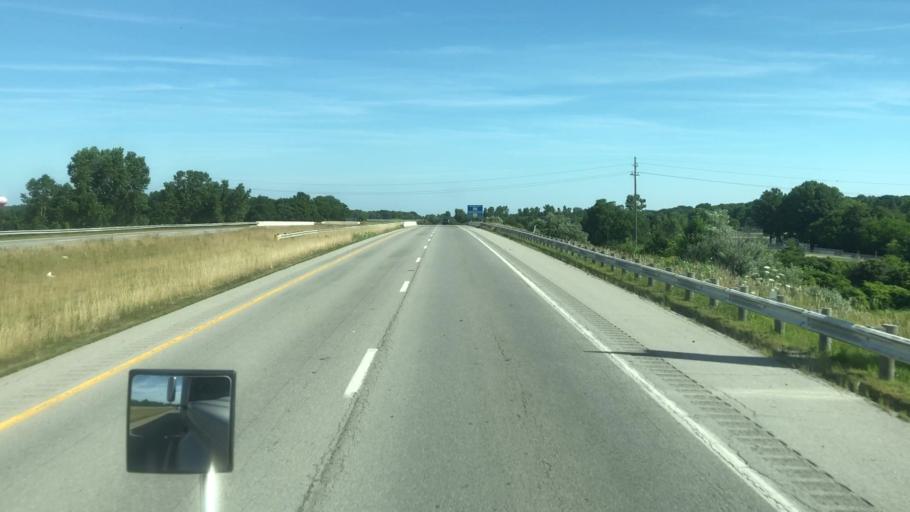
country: US
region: Ohio
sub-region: Erie County
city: Huron
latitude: 41.3909
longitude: -82.5739
